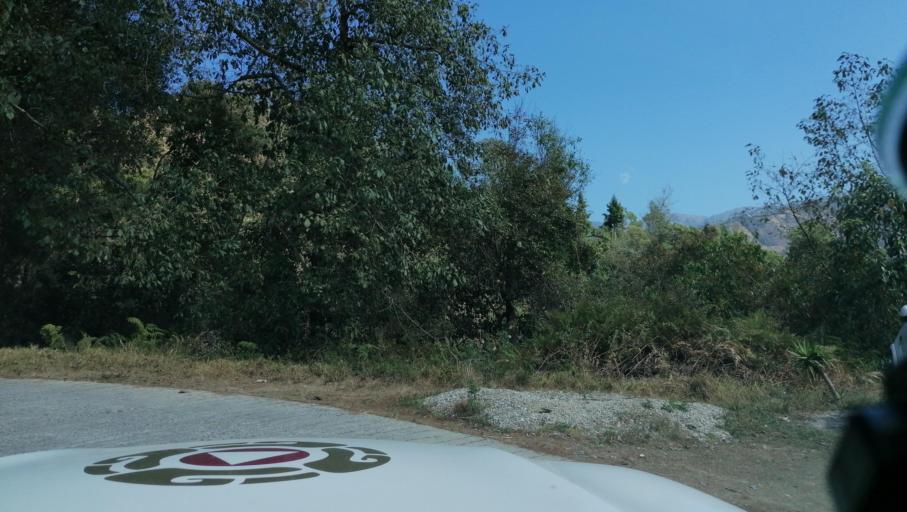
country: GT
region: San Marcos
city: Tacana
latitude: 15.2027
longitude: -92.2031
